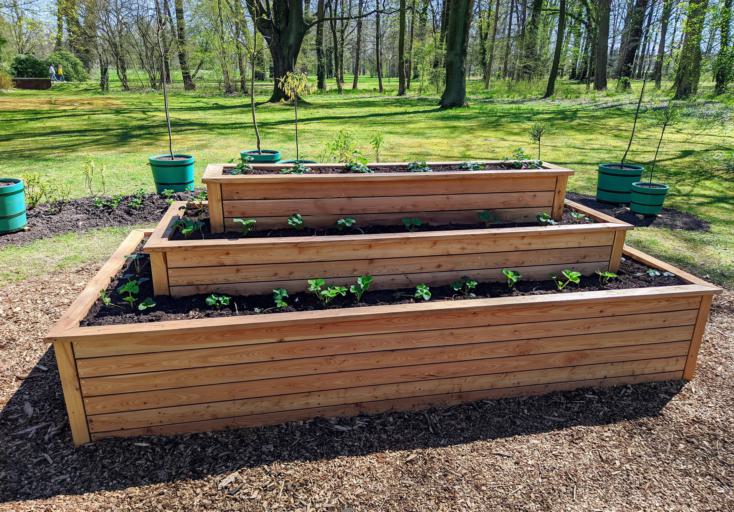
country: DE
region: Brandenburg
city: Cottbus
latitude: 51.7412
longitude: 14.3689
